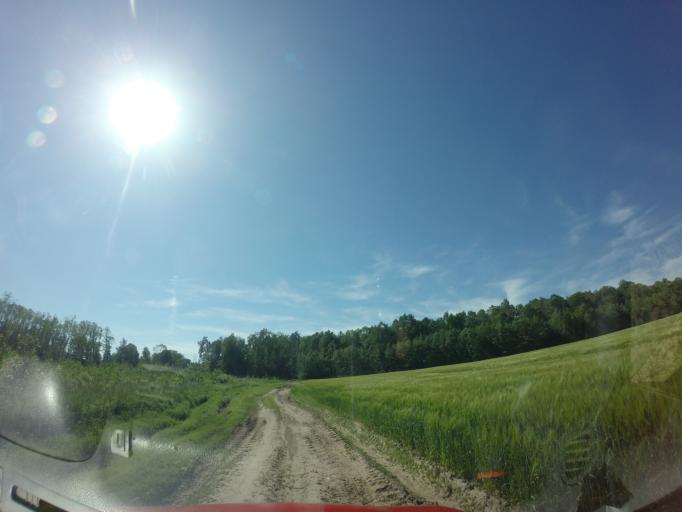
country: PL
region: West Pomeranian Voivodeship
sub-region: Powiat choszczenski
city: Choszczno
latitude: 53.1724
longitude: 15.3523
